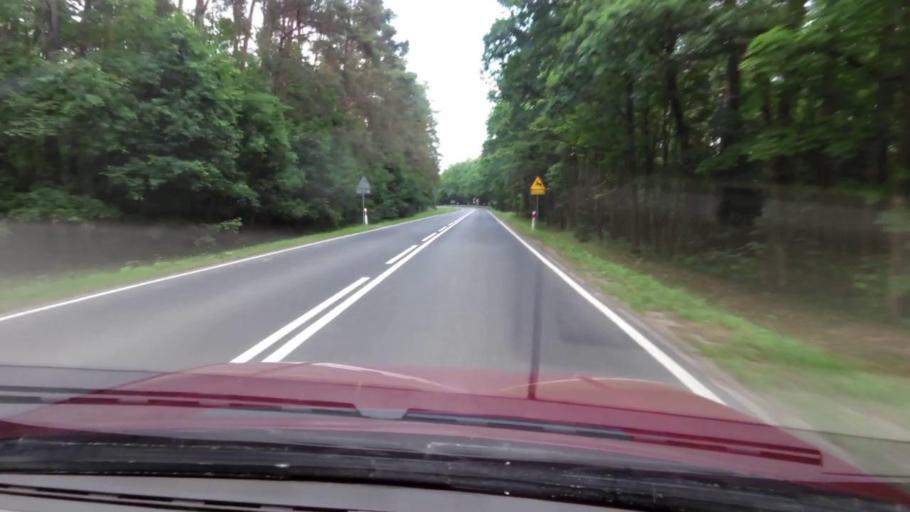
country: PL
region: Pomeranian Voivodeship
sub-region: Powiat bytowski
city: Trzebielino
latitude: 54.2528
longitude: 17.1036
